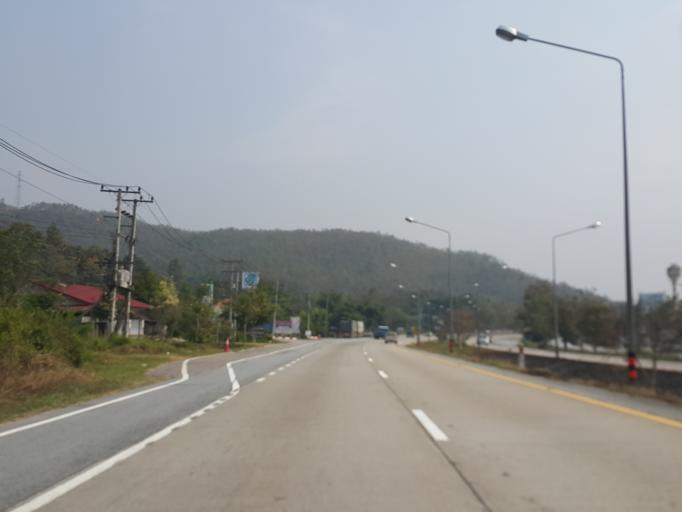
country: TH
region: Lamphun
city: Mae Tha
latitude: 18.4660
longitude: 99.1409
